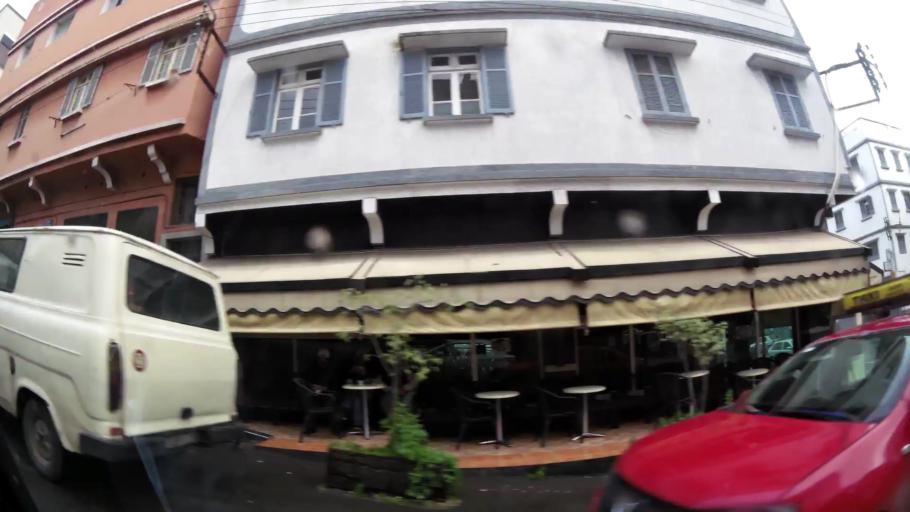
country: MA
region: Grand Casablanca
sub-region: Casablanca
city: Casablanca
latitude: 33.5503
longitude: -7.5797
